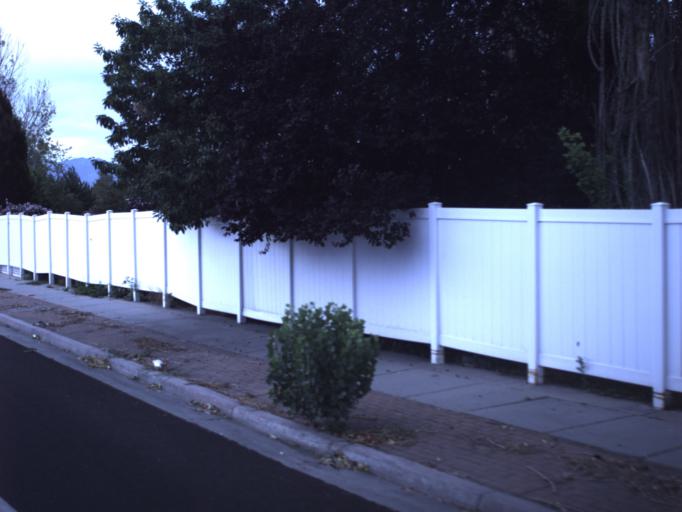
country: US
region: Utah
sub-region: Davis County
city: Clinton
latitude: 41.1636
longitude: -112.0710
